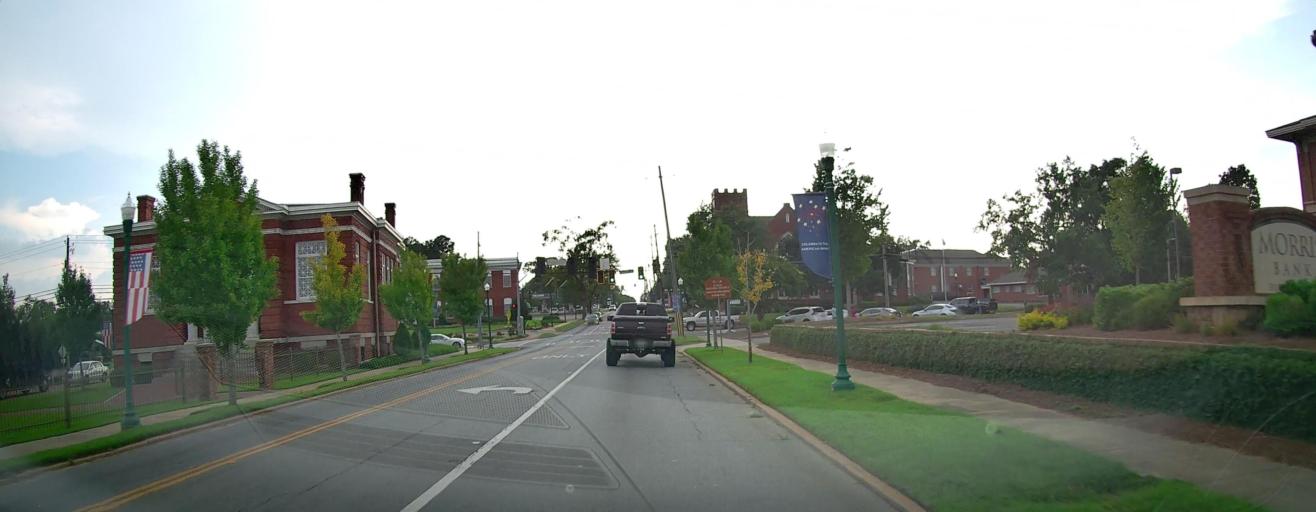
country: US
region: Georgia
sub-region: Laurens County
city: Dublin
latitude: 32.5389
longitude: -82.9079
